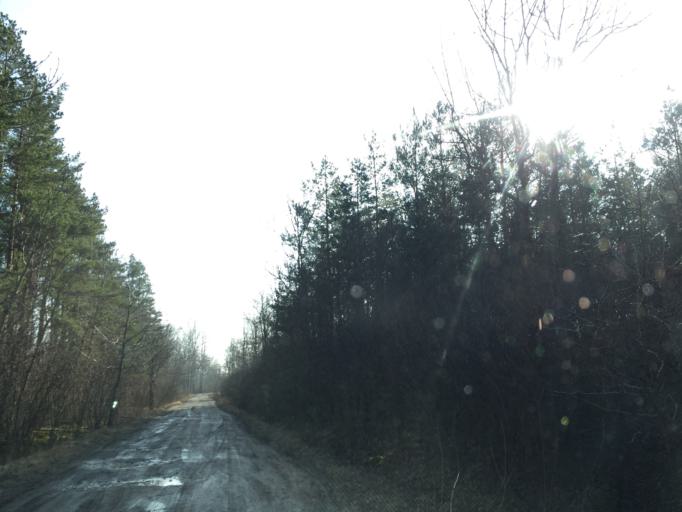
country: EE
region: Saare
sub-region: Kuressaare linn
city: Kuressaare
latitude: 58.2365
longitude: 22.4465
